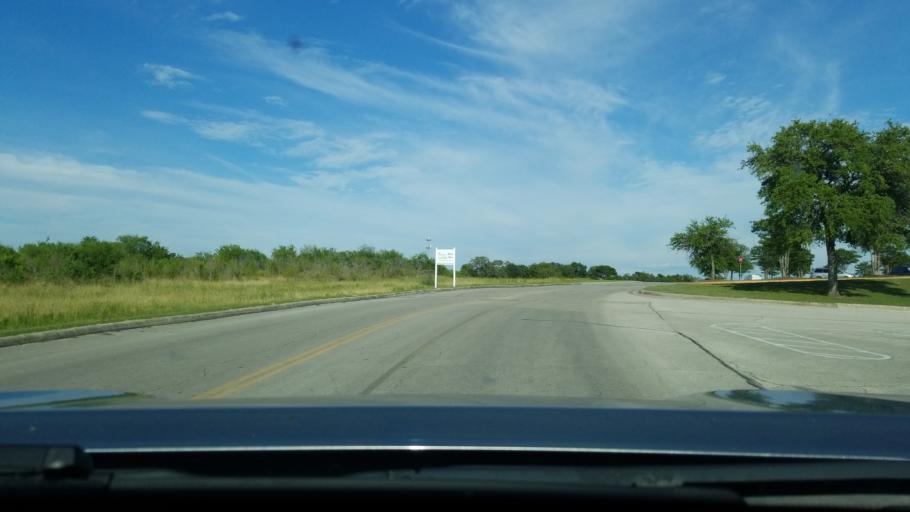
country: US
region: Texas
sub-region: Bexar County
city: Live Oak
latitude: 29.5991
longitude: -98.3507
